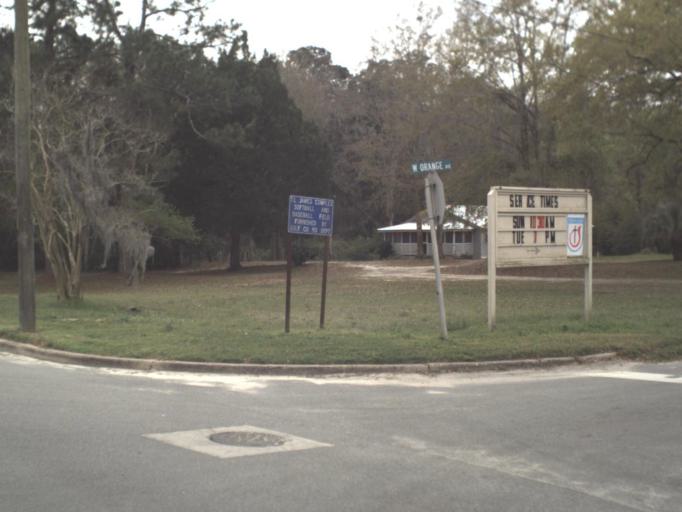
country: US
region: Florida
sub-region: Gulf County
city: Wewahitchka
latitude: 30.1034
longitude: -85.2007
